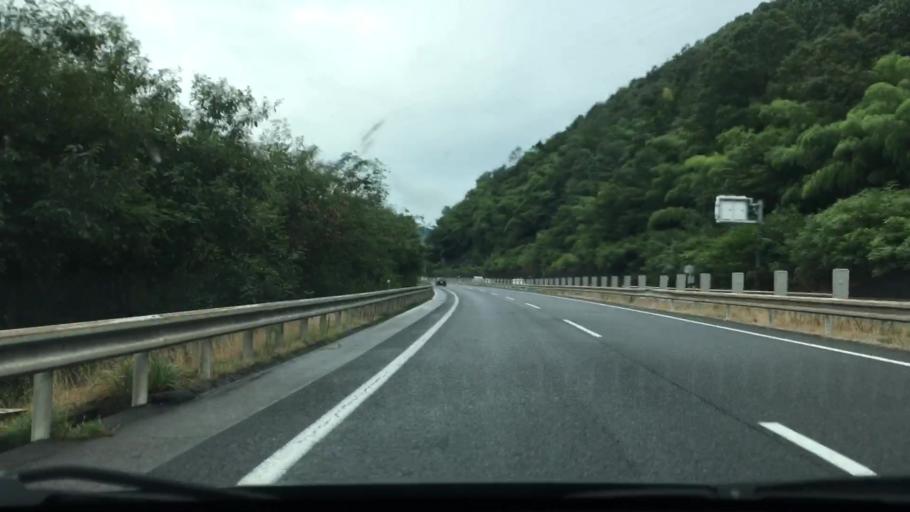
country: JP
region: Hiroshima
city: Hiroshima-shi
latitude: 34.5237
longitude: 132.4289
